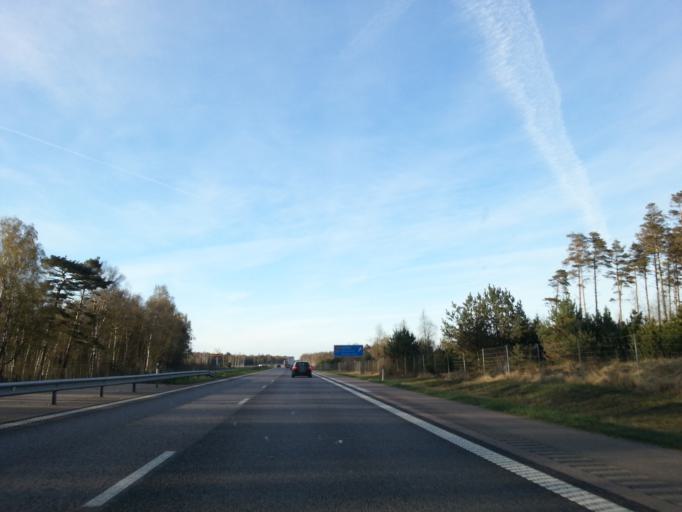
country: SE
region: Halland
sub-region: Laholms Kommun
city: Mellbystrand
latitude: 56.4978
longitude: 12.9575
